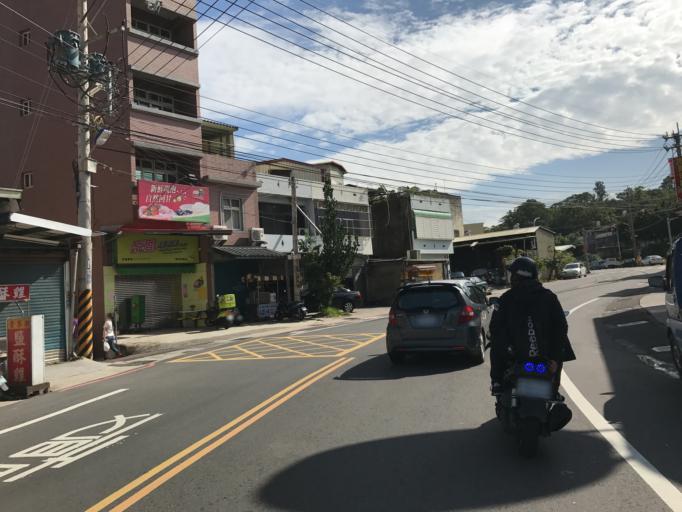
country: TW
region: Taiwan
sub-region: Hsinchu
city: Hsinchu
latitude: 24.7681
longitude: 120.9783
